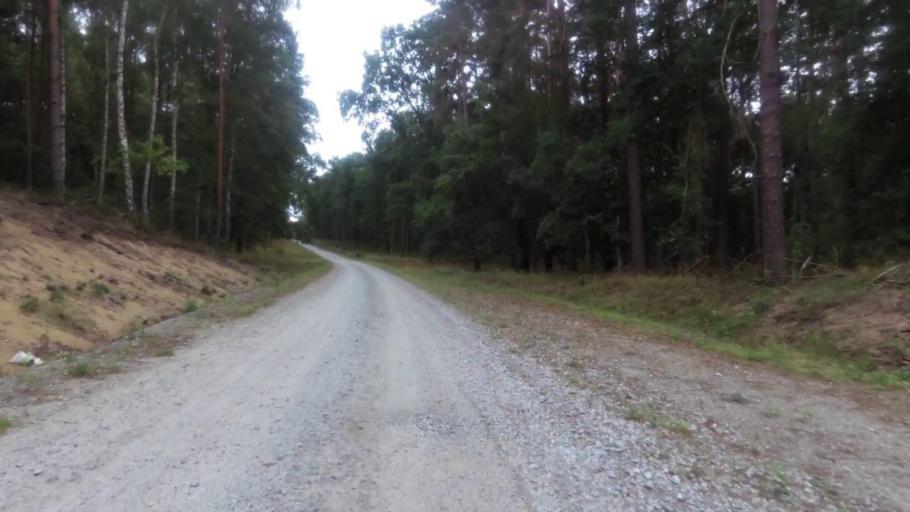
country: PL
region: Lubusz
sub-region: Powiat gorzowski
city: Kostrzyn nad Odra
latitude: 52.6422
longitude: 14.6430
